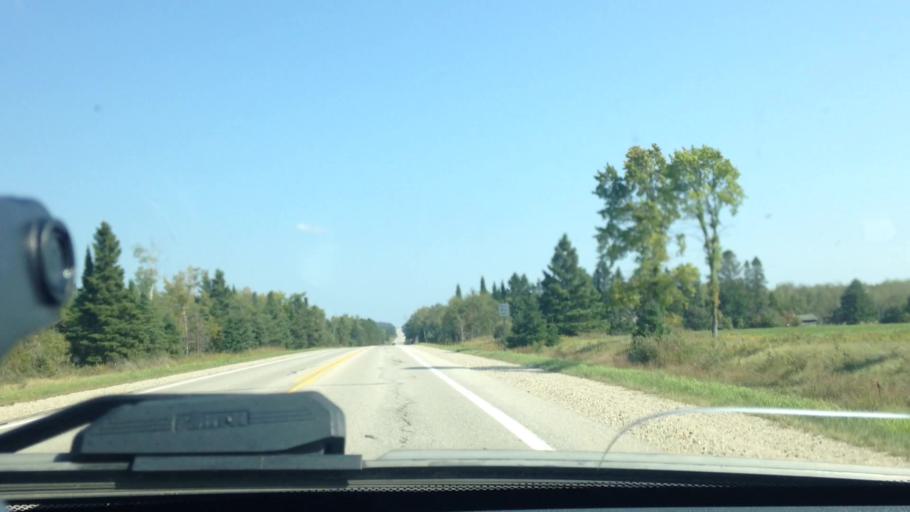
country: US
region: Michigan
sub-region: Luce County
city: Newberry
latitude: 46.3105
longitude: -85.5981
